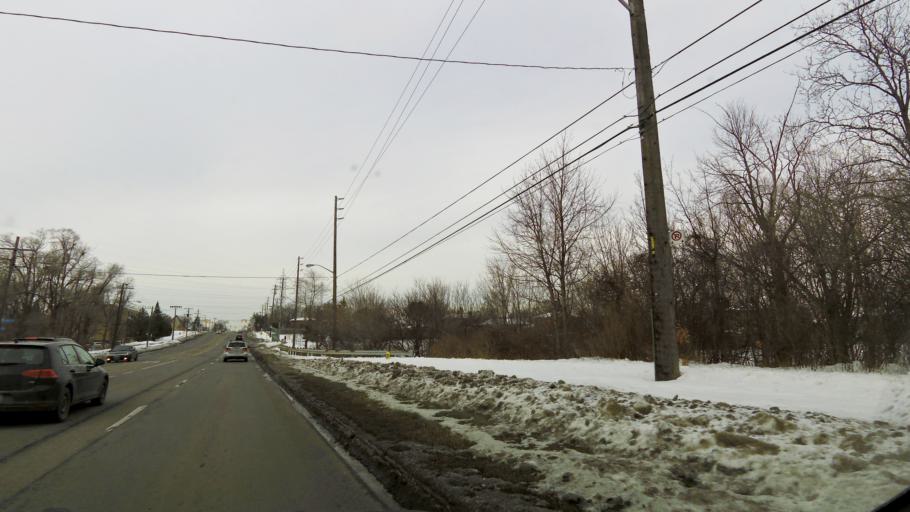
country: CA
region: Ontario
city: Etobicoke
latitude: 43.7196
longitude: -79.5571
